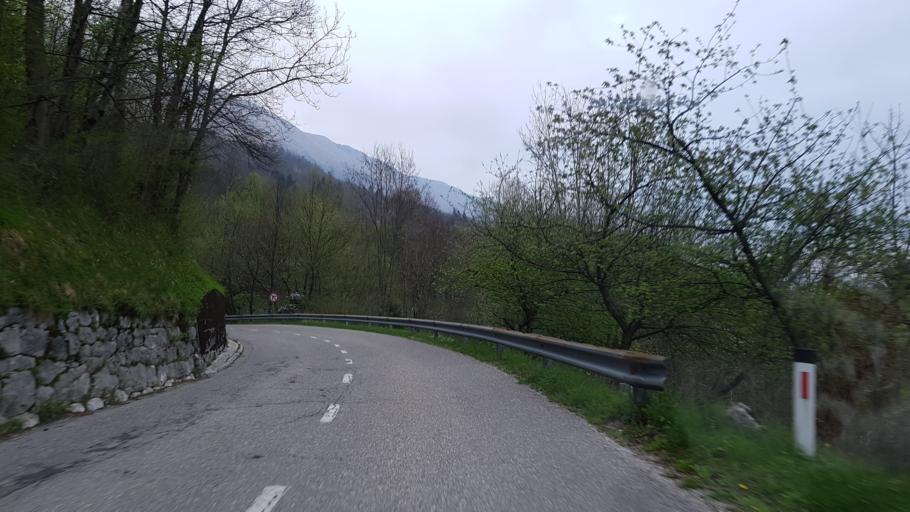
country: IT
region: Friuli Venezia Giulia
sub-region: Provincia di Udine
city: Pulfero
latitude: 46.2542
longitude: 13.4418
